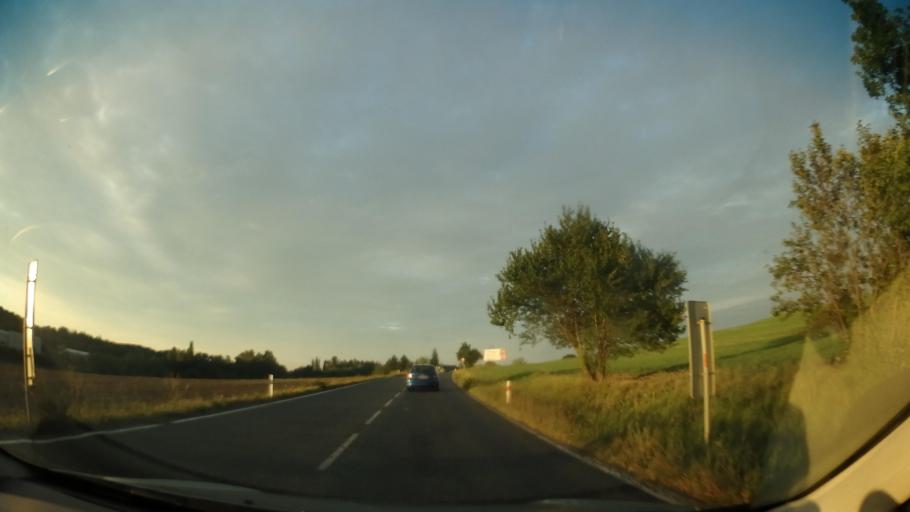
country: CZ
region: Central Bohemia
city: Milovice
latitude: 50.2218
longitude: 14.8760
